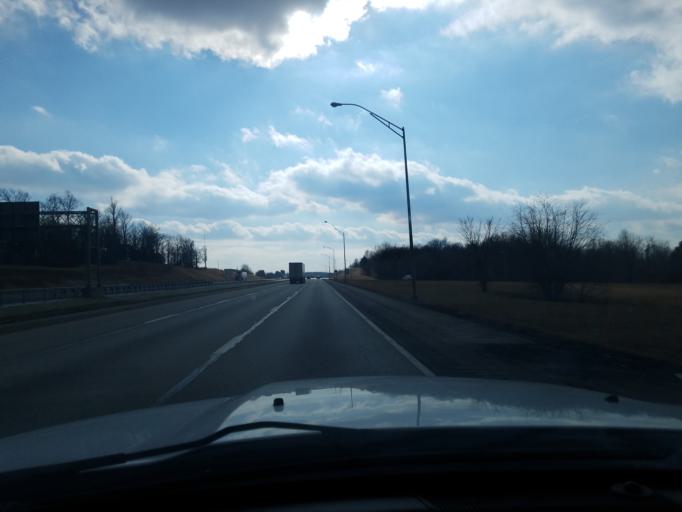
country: US
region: Kentucky
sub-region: Hardin County
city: Elizabethtown
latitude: 37.7001
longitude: -85.8360
